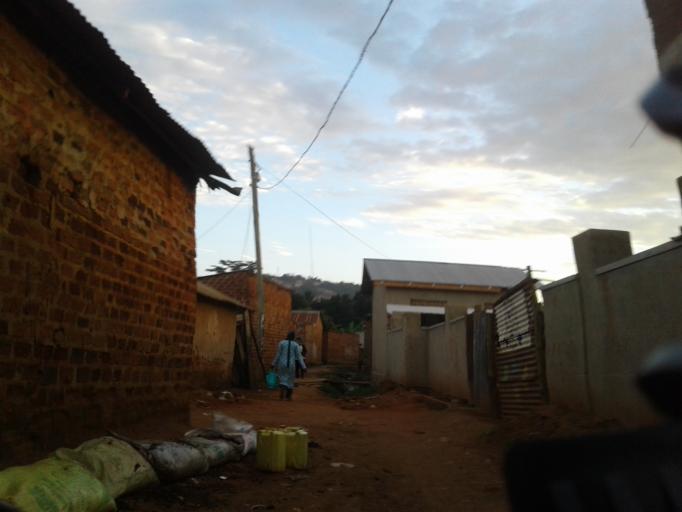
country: UG
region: Central Region
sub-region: Kampala District
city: Kampala
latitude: 0.2649
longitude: 32.6221
